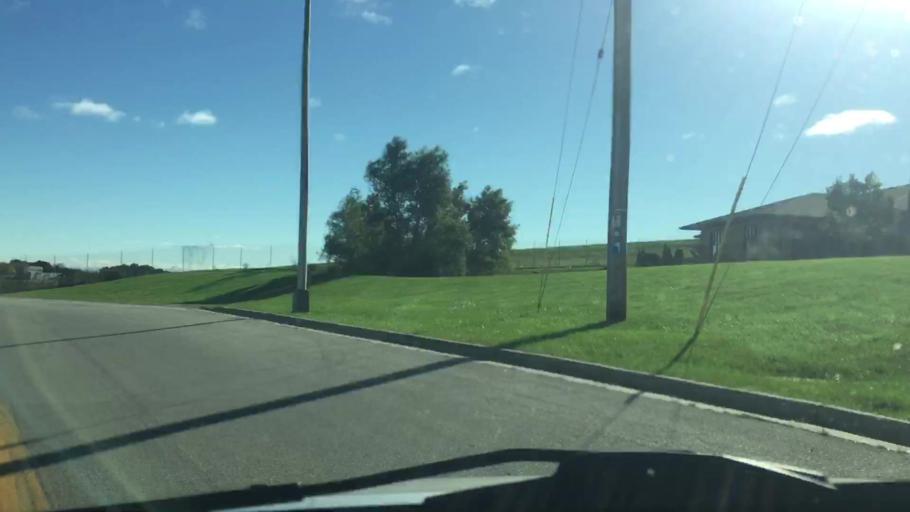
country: US
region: Wisconsin
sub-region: Waukesha County
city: Waukesha
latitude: 43.0427
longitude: -88.2542
